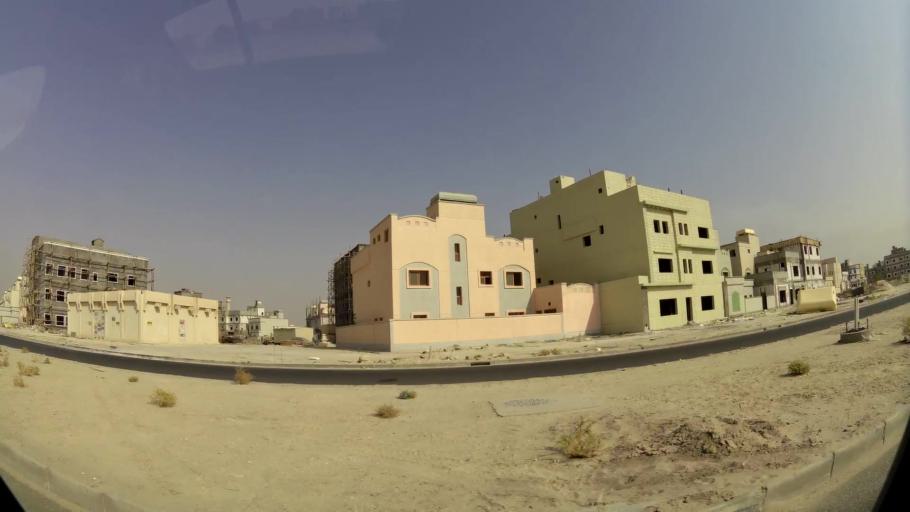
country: KW
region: Muhafazat al Jahra'
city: Al Jahra'
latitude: 29.3445
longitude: 47.7660
